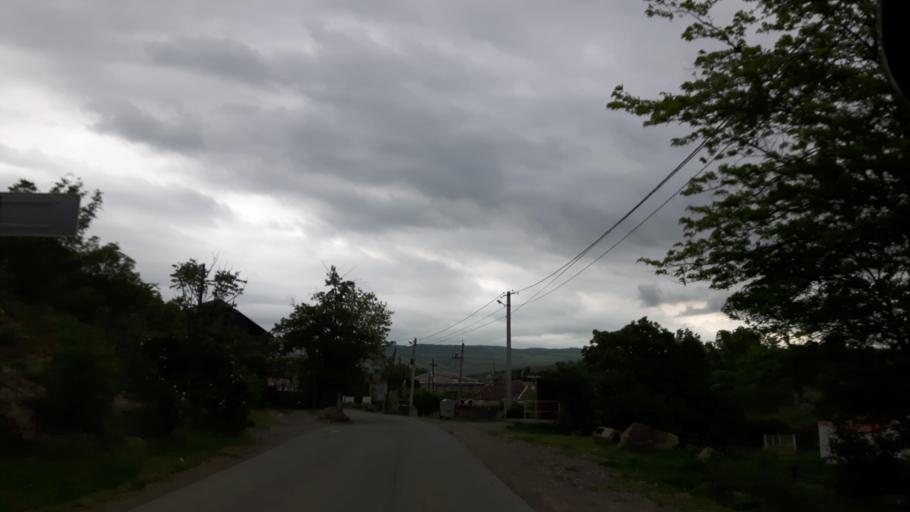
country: GE
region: Shida Kartli
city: Gori
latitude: 41.9372
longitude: 44.1182
